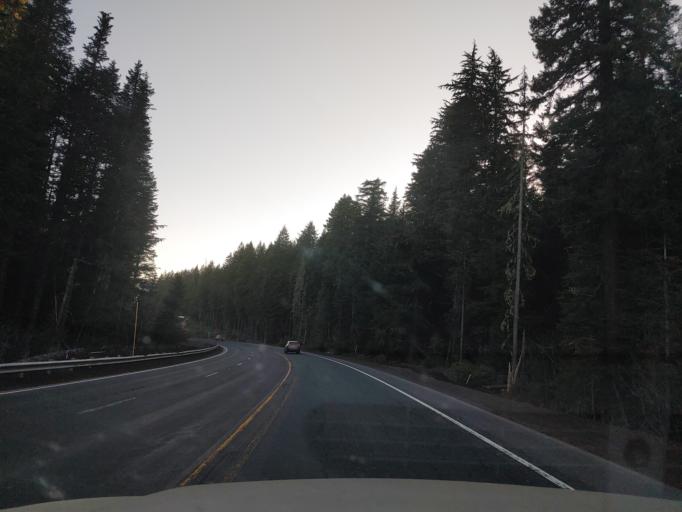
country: US
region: Oregon
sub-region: Lane County
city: Oakridge
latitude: 43.6161
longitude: -122.1004
